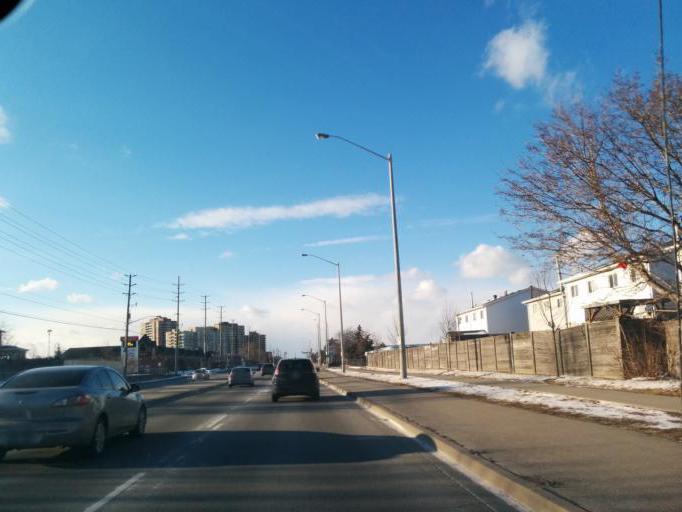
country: CA
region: Ontario
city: Brampton
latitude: 43.6494
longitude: -79.7340
